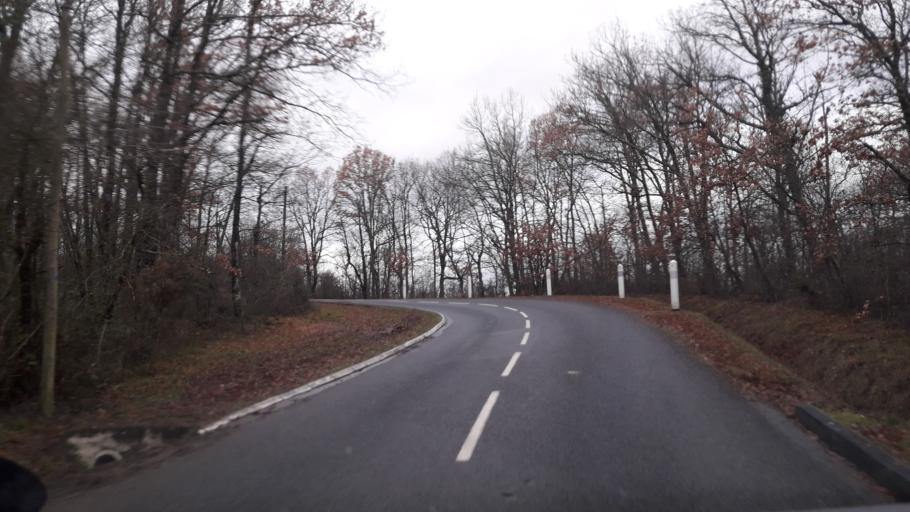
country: FR
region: Midi-Pyrenees
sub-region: Departement de la Haute-Garonne
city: Montesquieu-Volvestre
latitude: 43.2275
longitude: 1.2789
